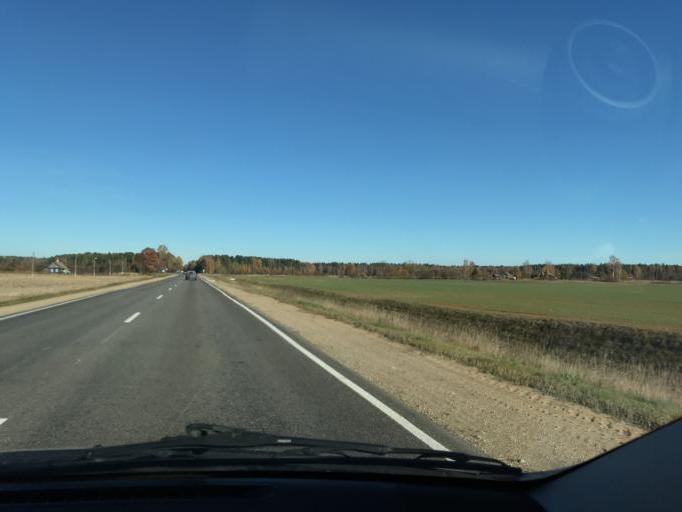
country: BY
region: Vitebsk
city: Lyepyel'
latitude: 55.0533
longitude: 28.7513
